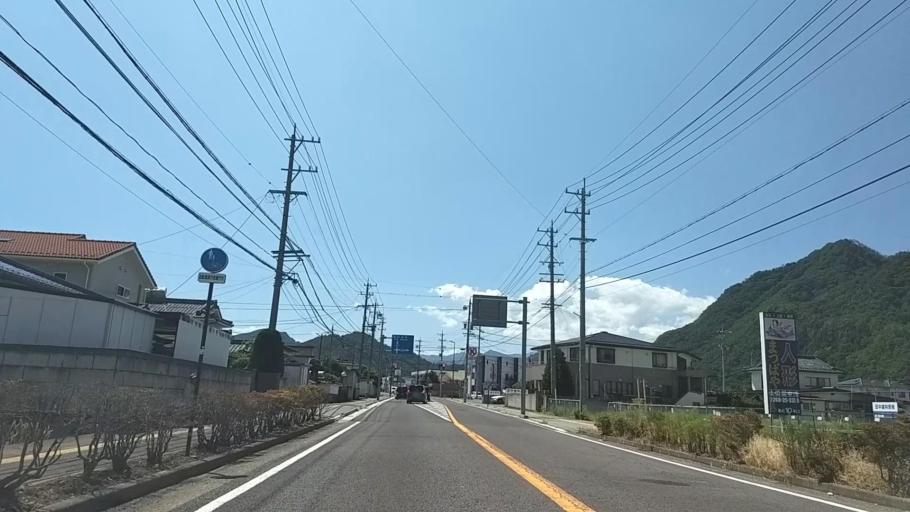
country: JP
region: Nagano
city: Kamimaruko
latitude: 36.3339
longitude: 138.2715
